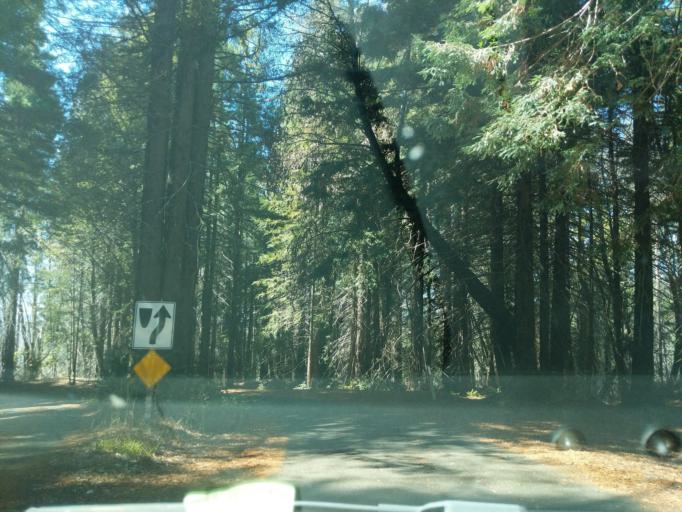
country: US
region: California
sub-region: Sonoma County
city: Monte Rio
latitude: 38.5252
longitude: -123.2307
